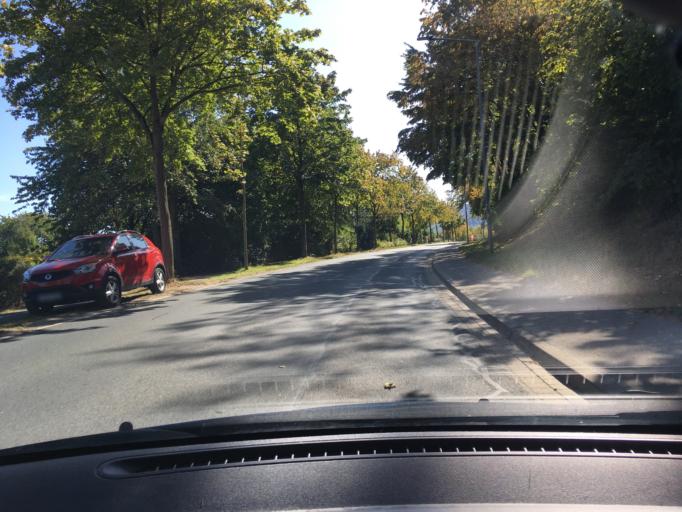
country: DE
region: Lower Saxony
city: Springe
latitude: 52.2149
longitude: 9.5679
